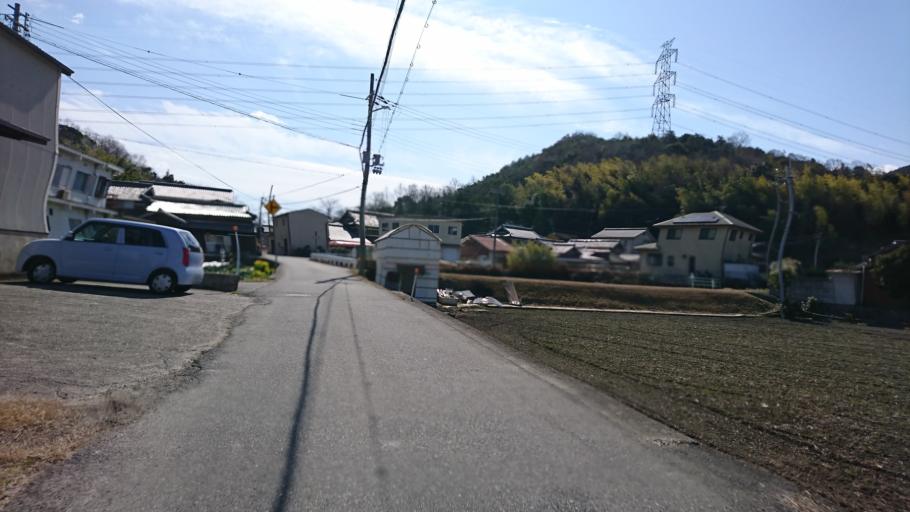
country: JP
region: Hyogo
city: Kakogawacho-honmachi
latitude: 34.8030
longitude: 134.8090
